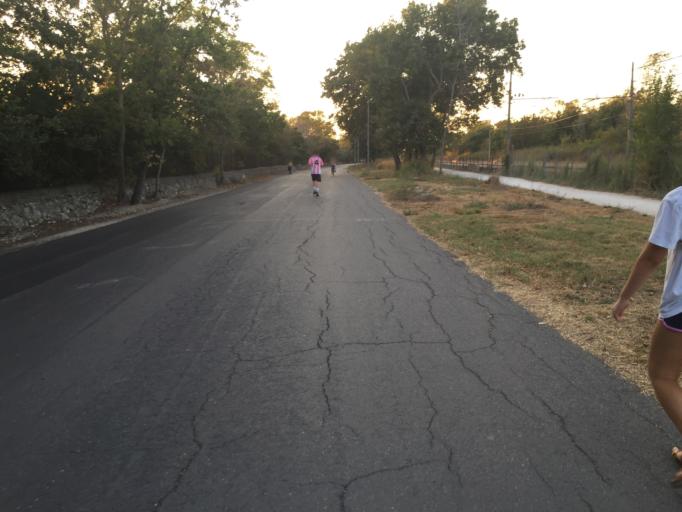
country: IT
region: Latium
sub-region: Citta metropolitana di Roma Capitale
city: Marina San Nicola
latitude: 41.9405
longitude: 12.1000
